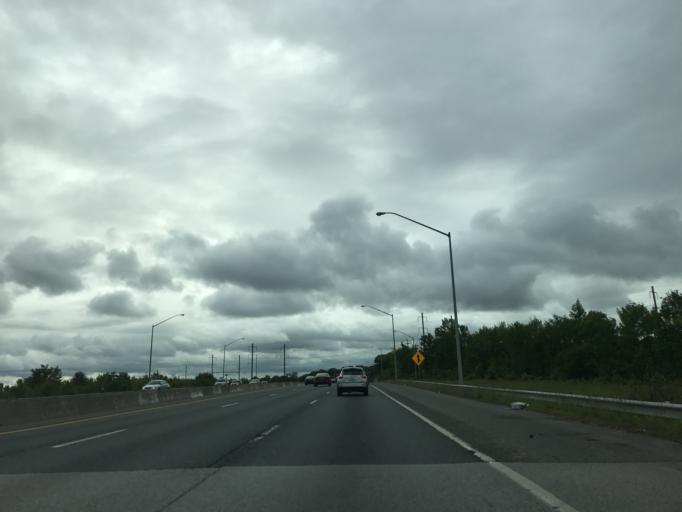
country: US
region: Maryland
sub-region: Prince George's County
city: Woodlawn
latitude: 38.9444
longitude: -76.8735
